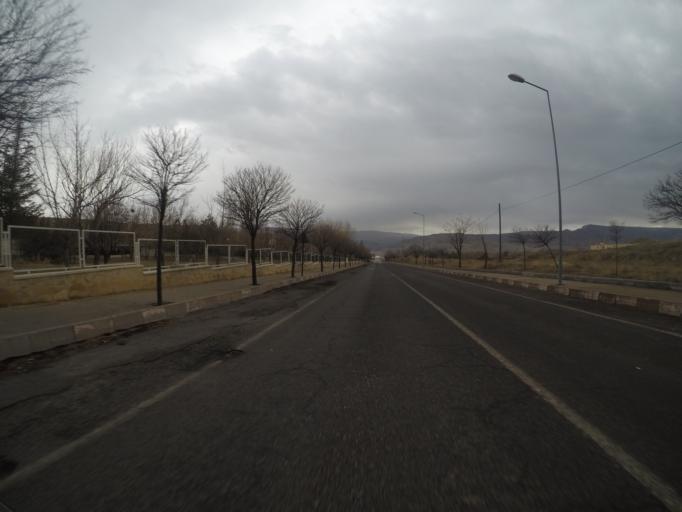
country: TR
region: Nevsehir
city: Urgub
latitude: 38.6334
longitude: 34.9007
